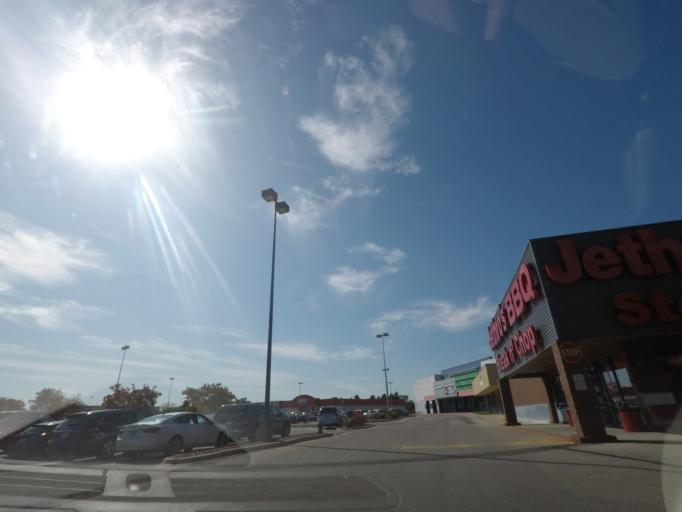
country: US
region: Iowa
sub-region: Story County
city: Ames
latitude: 42.0114
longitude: -93.6124
